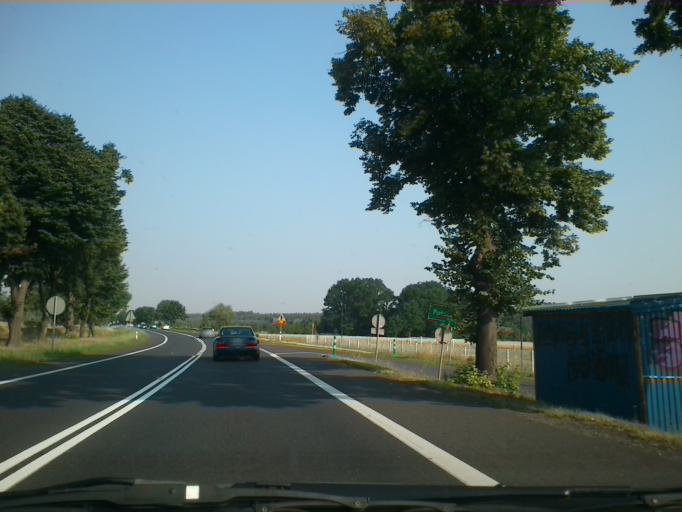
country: PL
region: Lower Silesian Voivodeship
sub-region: Powiat polkowicki
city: Radwanice
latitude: 51.5693
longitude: 16.0133
